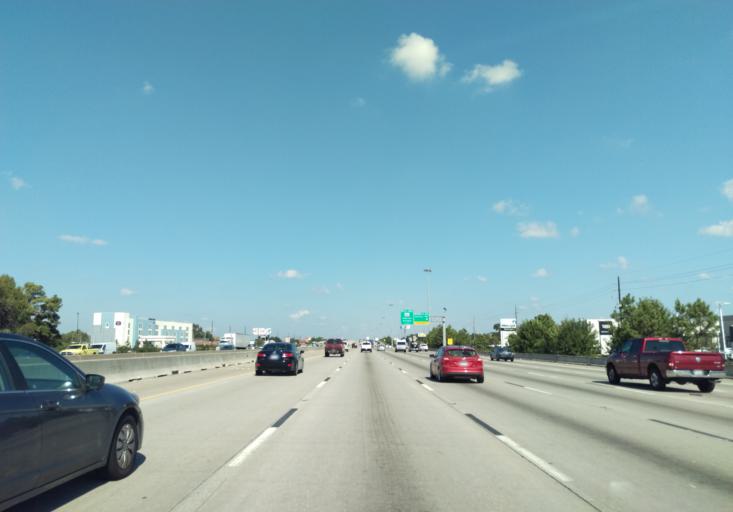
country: US
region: Texas
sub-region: Harris County
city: Aldine
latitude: 29.9909
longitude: -95.4242
